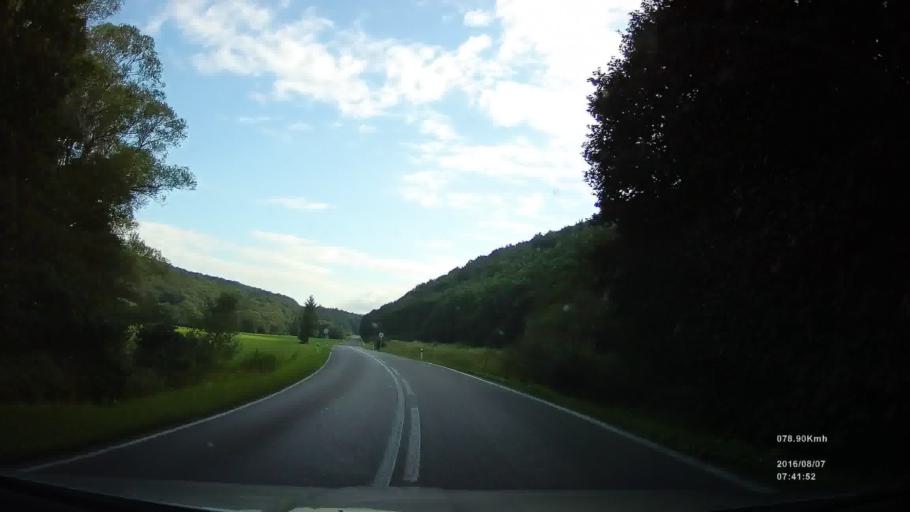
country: SK
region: Presovsky
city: Stropkov
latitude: 49.2570
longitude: 21.6927
